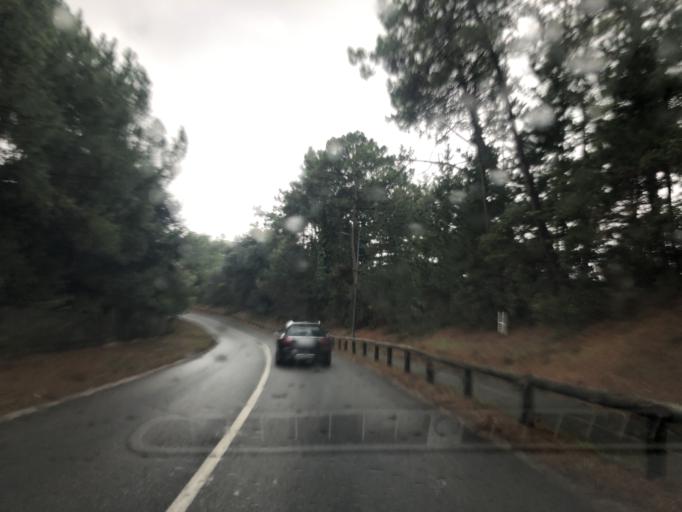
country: FR
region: Aquitaine
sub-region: Departement de la Gironde
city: Arcachon
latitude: 44.6920
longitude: -1.2390
